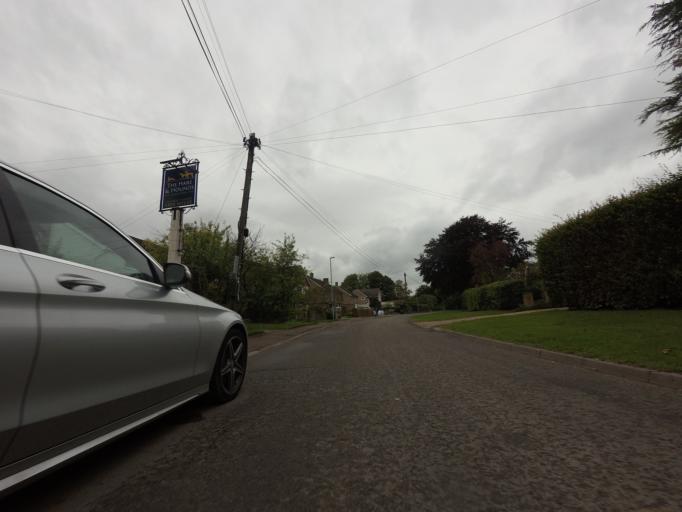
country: GB
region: England
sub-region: Cambridgeshire
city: Haslingfield
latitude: 52.1518
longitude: 0.0282
